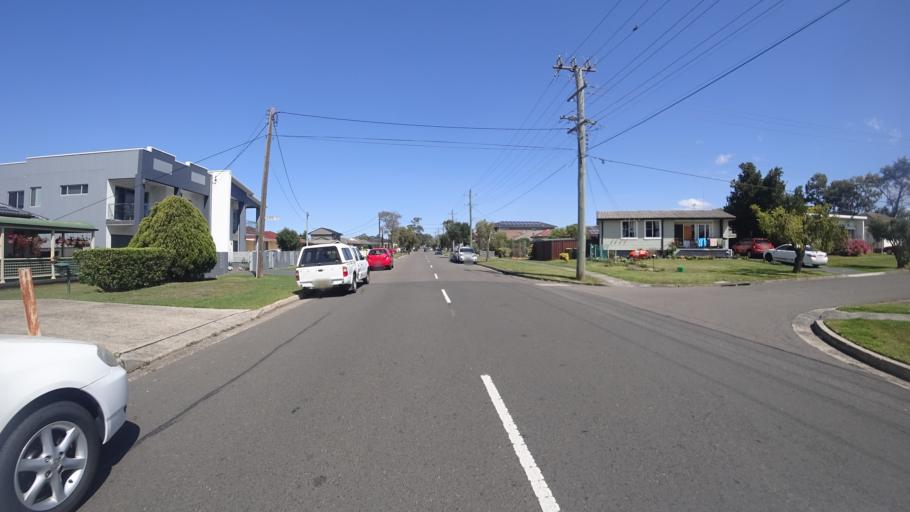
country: AU
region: New South Wales
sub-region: Liverpool
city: Miller
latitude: -33.9354
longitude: 150.8997
